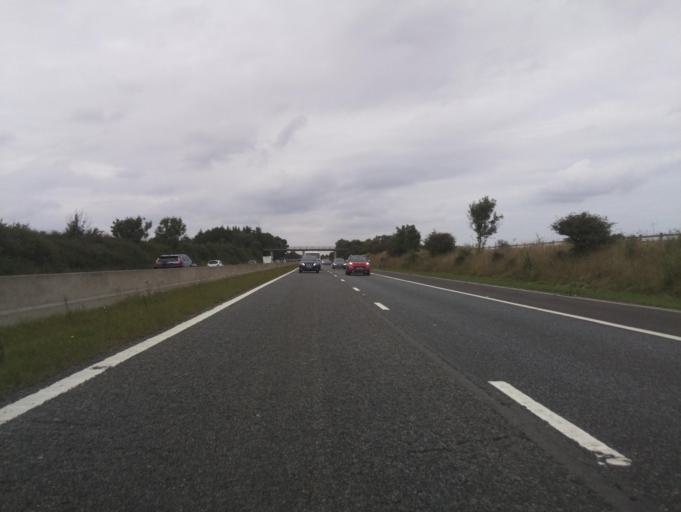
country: GB
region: England
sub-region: County Durham
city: West Rainton
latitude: 54.8253
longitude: -1.5232
